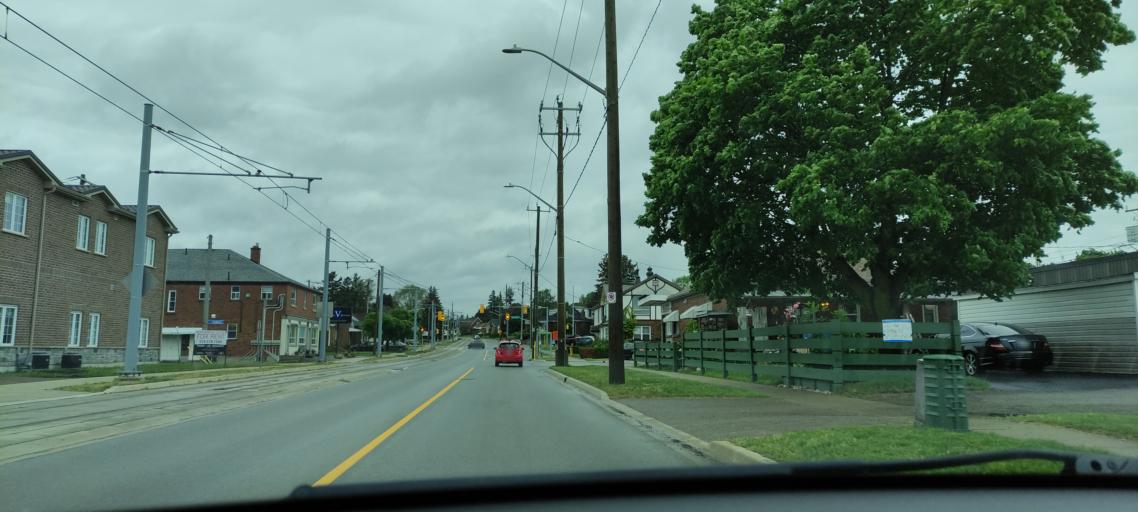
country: CA
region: Ontario
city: Kitchener
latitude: 43.4380
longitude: -80.4758
